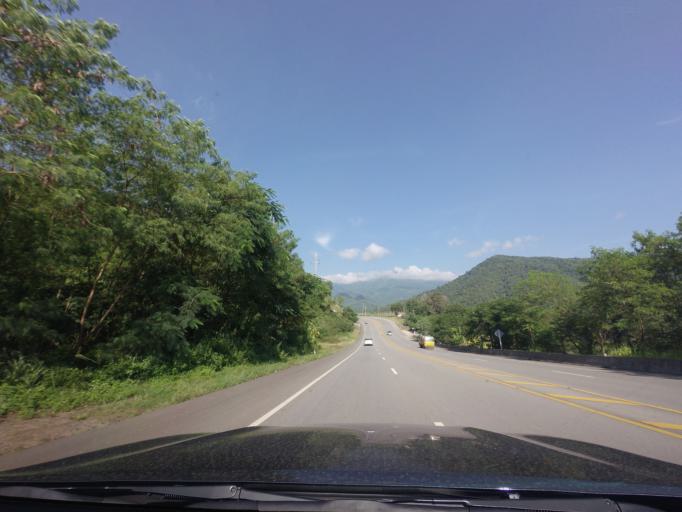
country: TH
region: Phetchabun
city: Lom Sak
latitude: 16.7783
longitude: 101.1102
